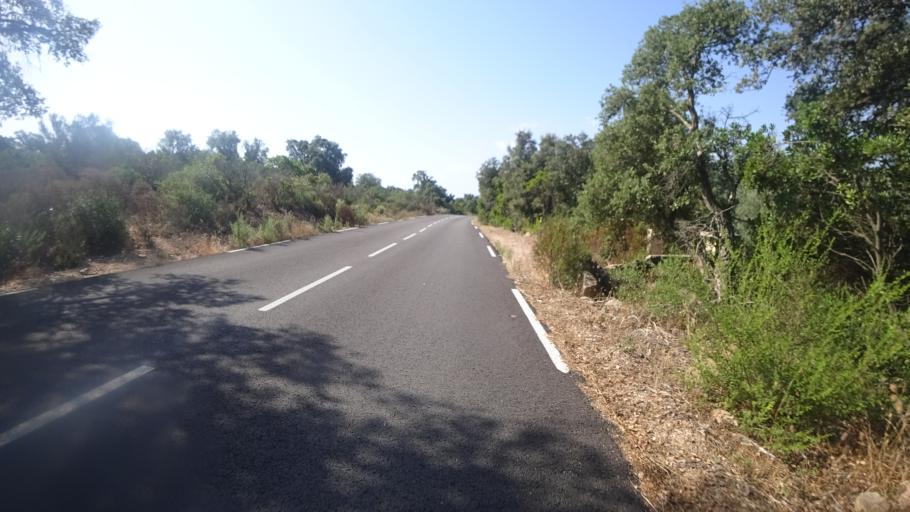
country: FR
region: Corsica
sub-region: Departement de la Corse-du-Sud
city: Porto-Vecchio
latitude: 41.6562
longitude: 9.3257
